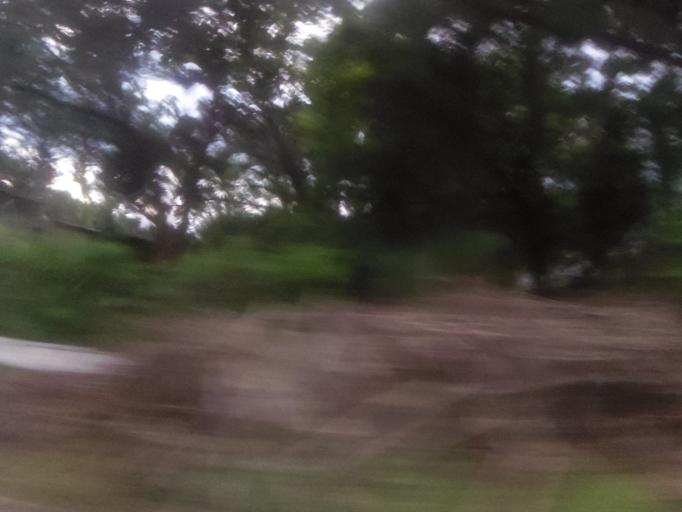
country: US
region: Florida
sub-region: Duval County
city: Jacksonville
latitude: 30.2983
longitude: -81.7086
